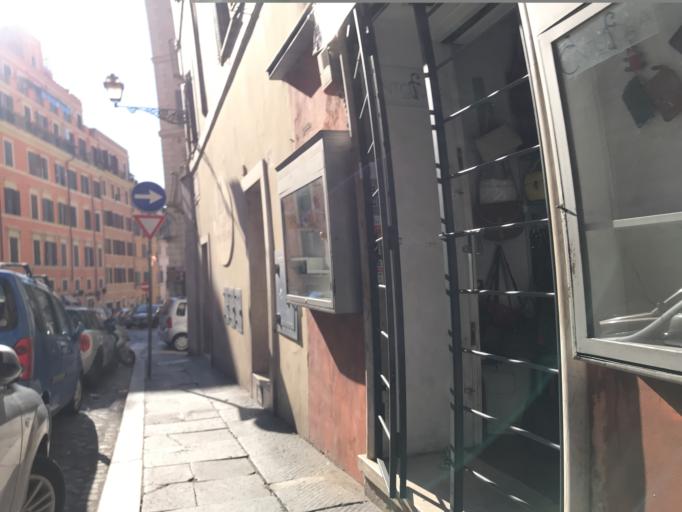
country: IT
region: Latium
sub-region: Citta metropolitana di Roma Capitale
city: Rome
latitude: 41.9051
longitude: 12.4859
